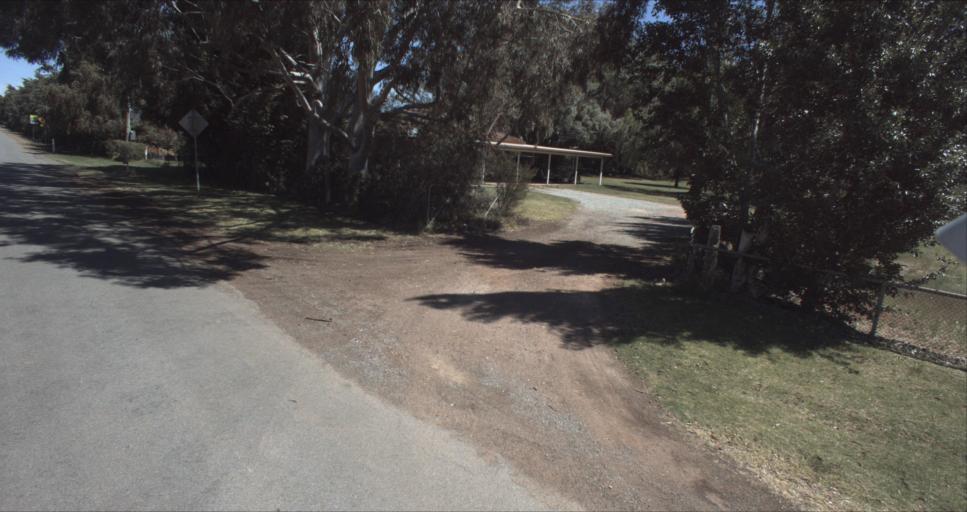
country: AU
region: New South Wales
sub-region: Leeton
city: Leeton
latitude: -34.5230
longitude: 146.3305
